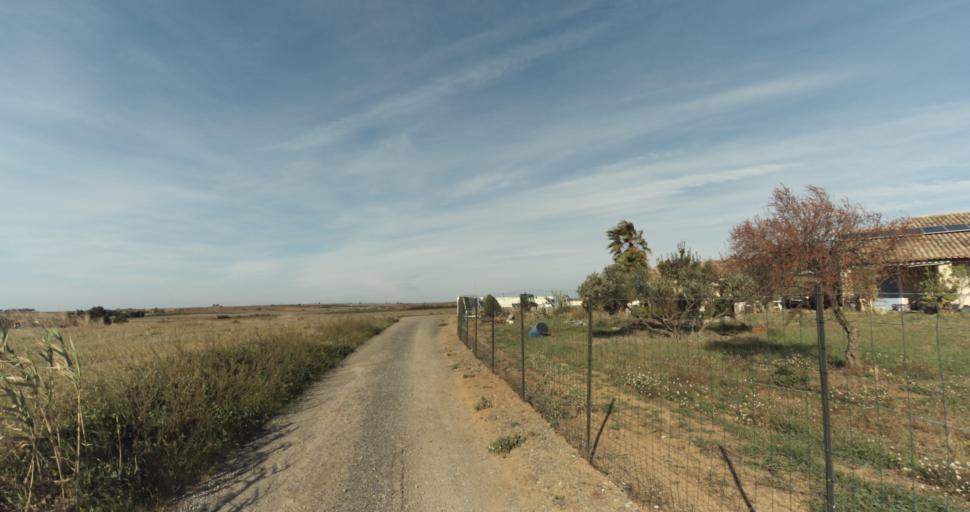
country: FR
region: Languedoc-Roussillon
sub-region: Departement de l'Herault
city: Marseillan
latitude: 43.3599
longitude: 3.5152
